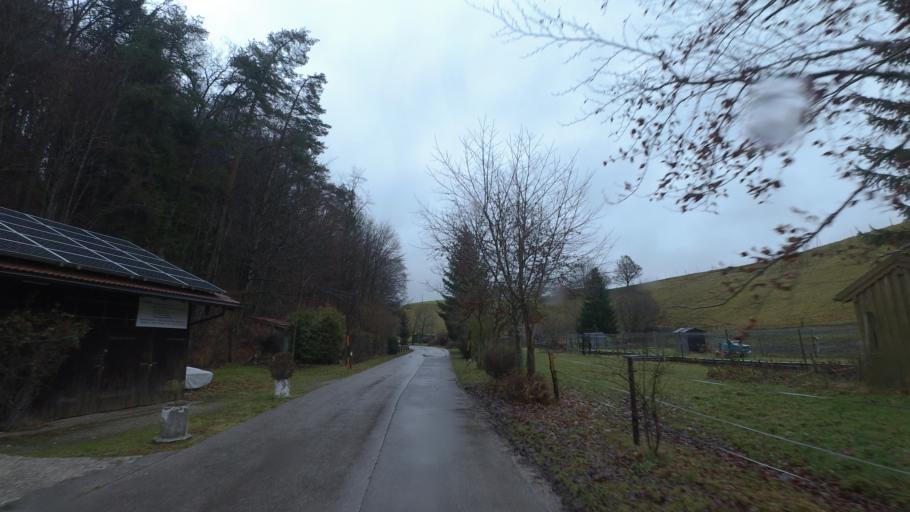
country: DE
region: Bavaria
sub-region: Upper Bavaria
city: Nussdorf
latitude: 47.9170
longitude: 12.6292
